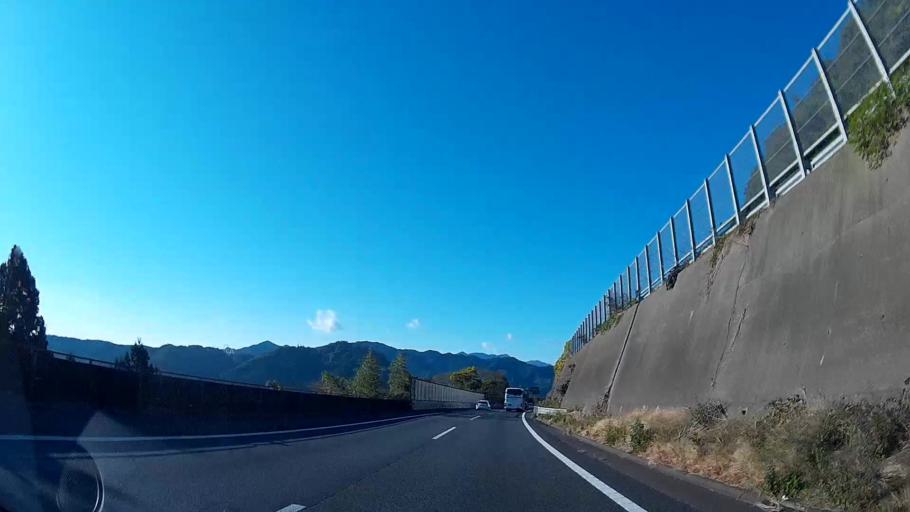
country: JP
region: Yamanashi
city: Uenohara
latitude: 35.6261
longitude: 139.2024
